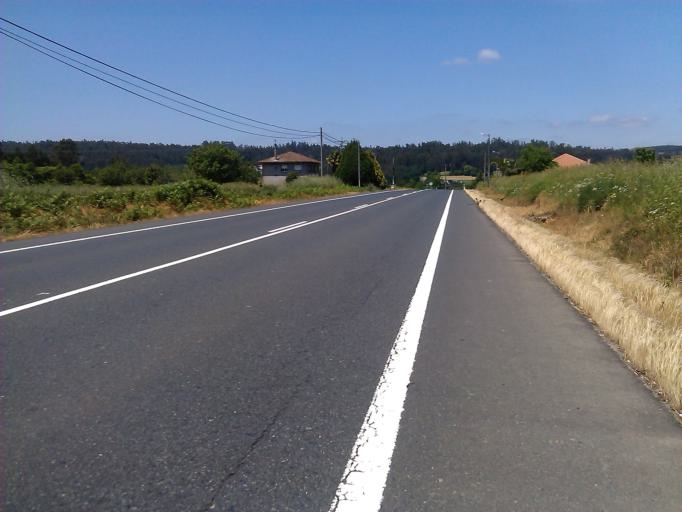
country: ES
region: Galicia
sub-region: Provincia da Coruna
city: Touro
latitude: 42.9013
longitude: -8.3863
